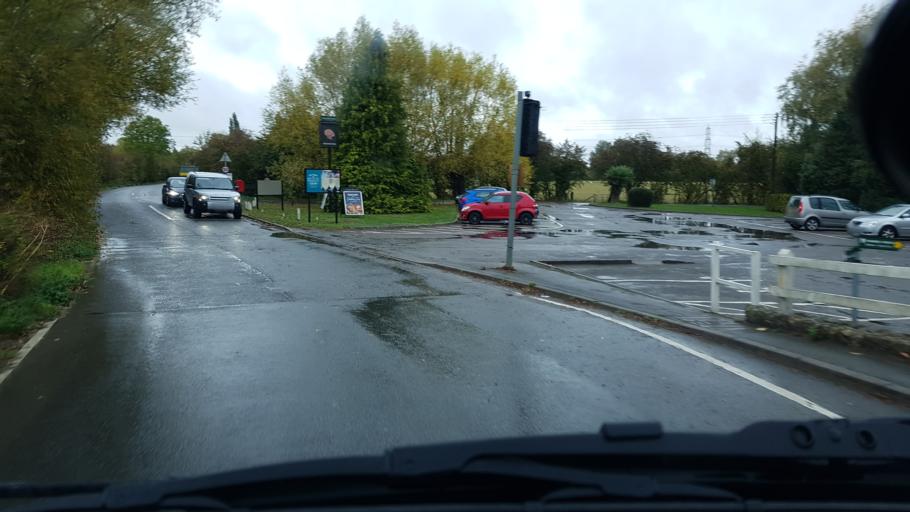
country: GB
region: England
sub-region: Oxfordshire
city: Frilford
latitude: 51.7101
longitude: -1.4172
